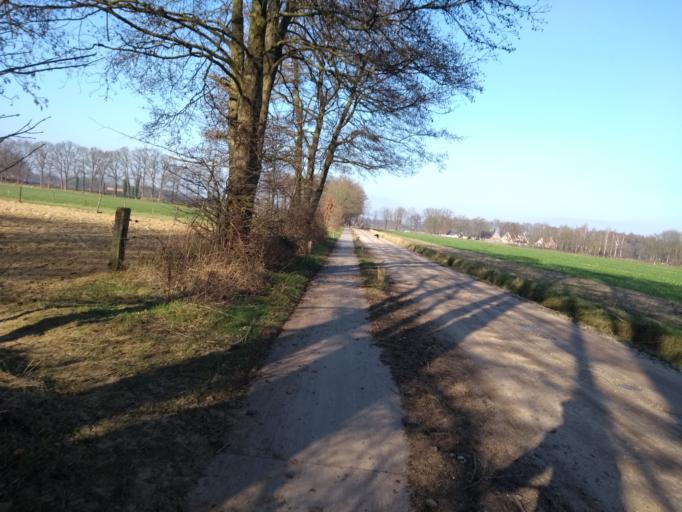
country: NL
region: Overijssel
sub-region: Gemeente Tubbergen
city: Tubbergen
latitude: 52.3955
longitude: 6.7383
